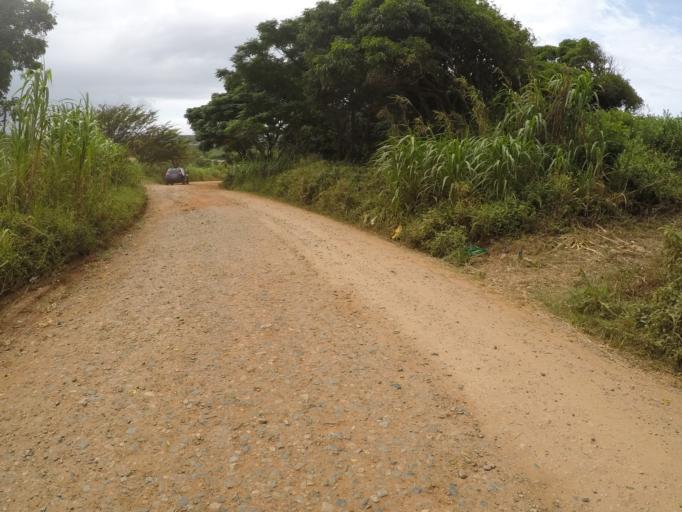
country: ZA
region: KwaZulu-Natal
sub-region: uThungulu District Municipality
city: eSikhawini
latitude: -28.8557
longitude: 31.9141
